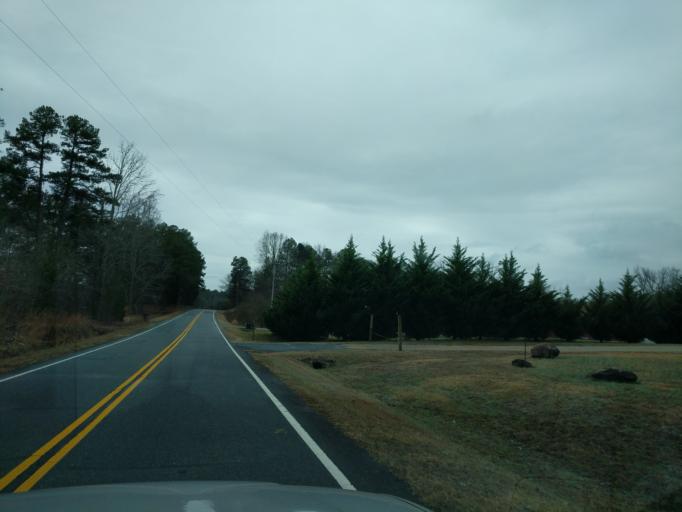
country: US
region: South Carolina
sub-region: Oconee County
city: Walhalla
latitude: 34.8014
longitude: -83.0763
